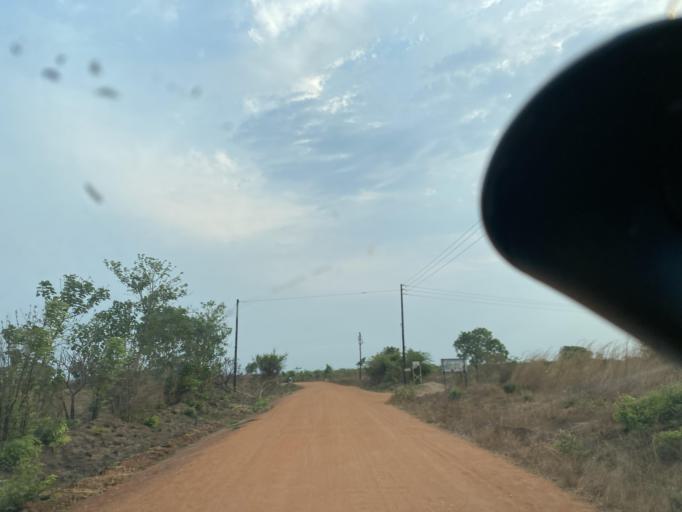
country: ZM
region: Lusaka
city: Chongwe
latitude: -15.2309
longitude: 28.5882
